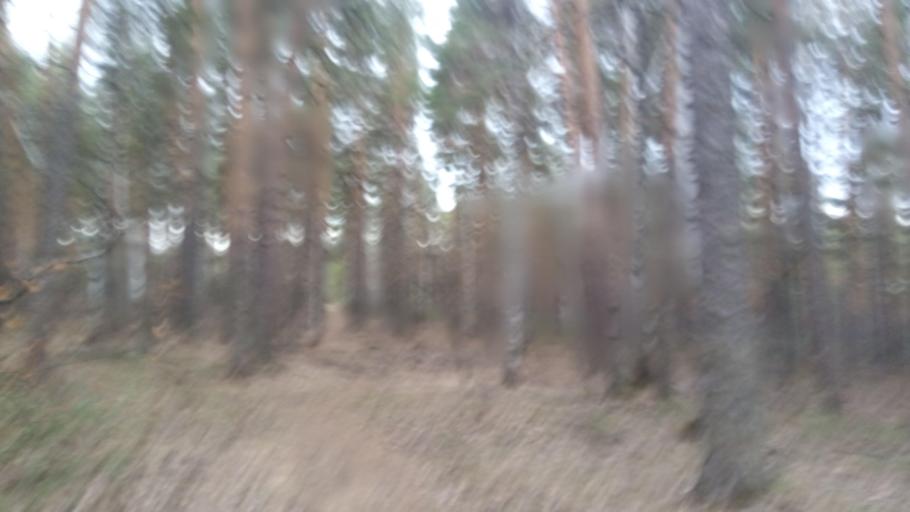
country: RU
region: Chelyabinsk
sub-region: Gorod Chelyabinsk
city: Chelyabinsk
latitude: 55.1370
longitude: 61.3390
